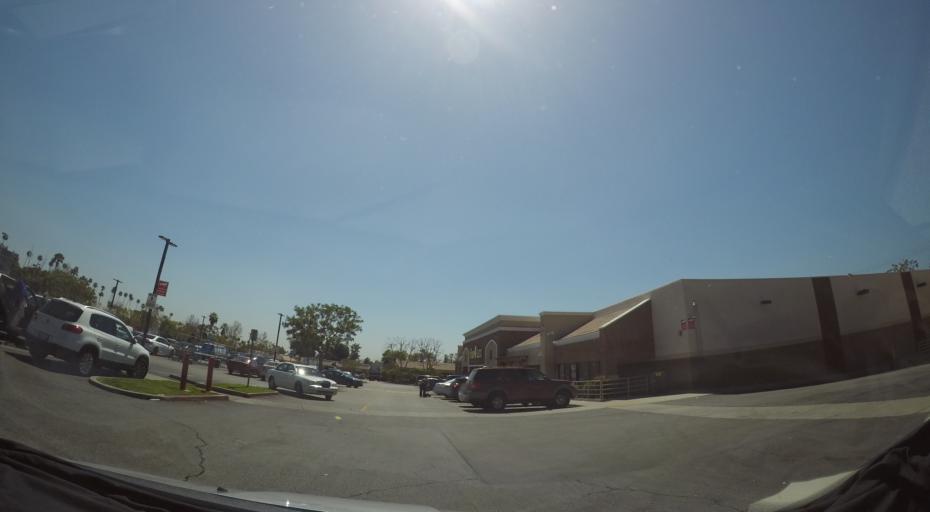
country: US
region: California
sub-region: Los Angeles County
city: Altadena
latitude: 34.1688
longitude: -118.1331
